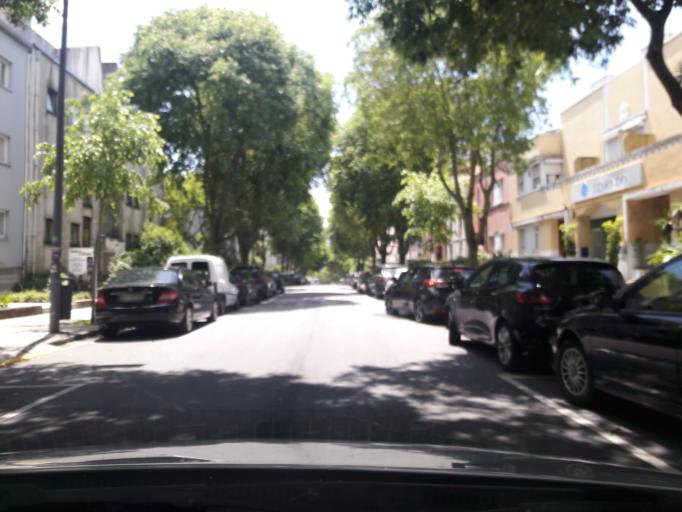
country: PT
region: Porto
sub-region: Porto
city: Porto
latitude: 41.1541
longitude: -8.6307
